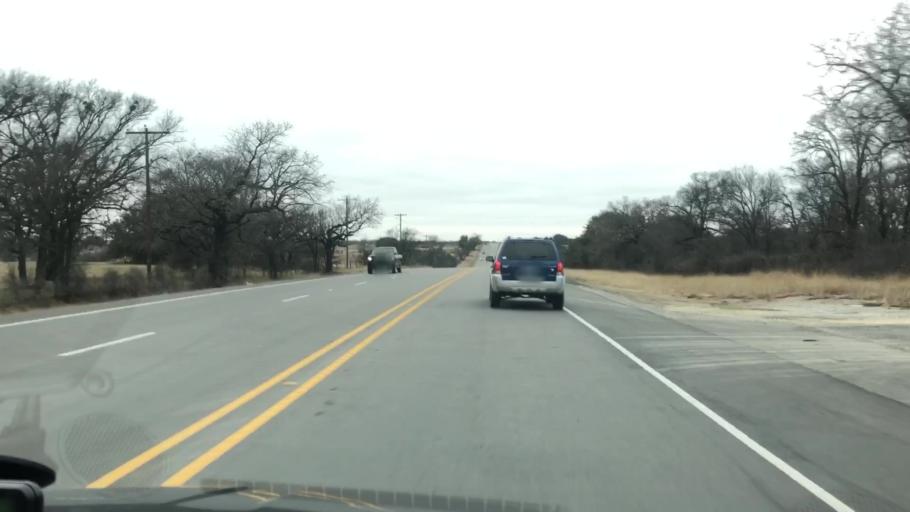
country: US
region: Texas
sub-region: Hamilton County
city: Hico
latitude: 32.0140
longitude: -98.0648
